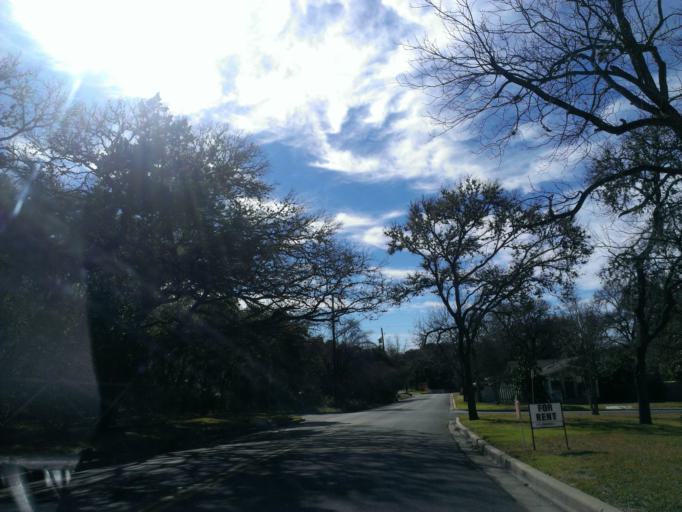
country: US
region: Texas
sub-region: Travis County
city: Rollingwood
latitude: 30.2968
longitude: -97.7753
